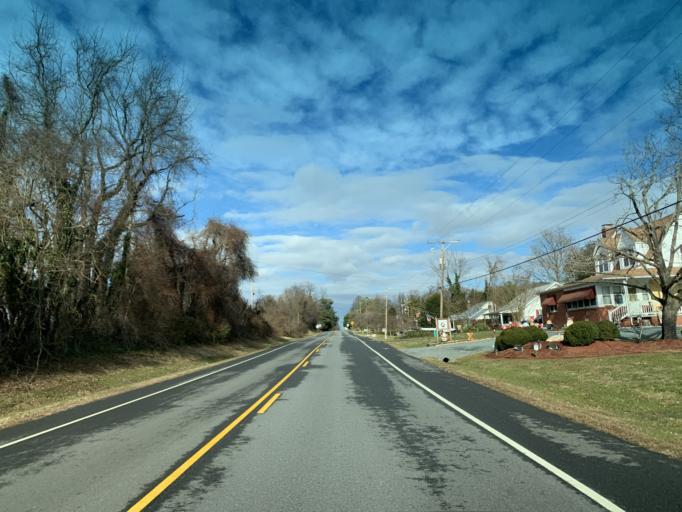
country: US
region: Maryland
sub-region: Harford County
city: Aberdeen Proving Ground
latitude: 39.3599
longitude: -76.0624
